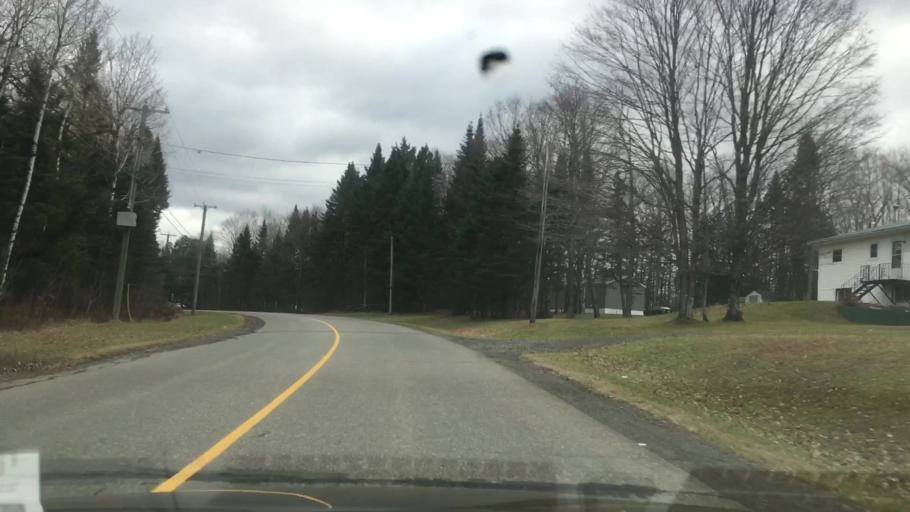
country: US
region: Maine
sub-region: Aroostook County
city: Fort Fairfield
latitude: 46.7481
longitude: -67.7488
